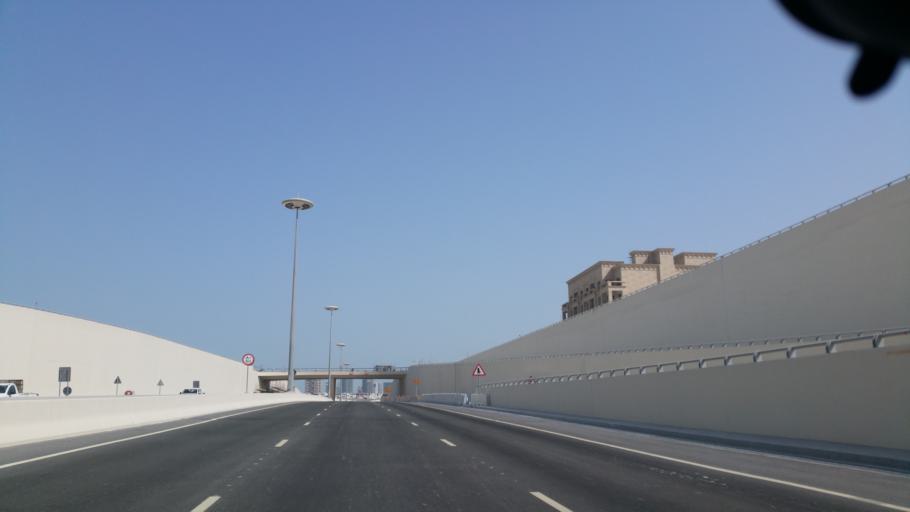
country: QA
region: Baladiyat Umm Salal
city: Umm Salal Muhammad
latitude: 25.4135
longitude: 51.5078
